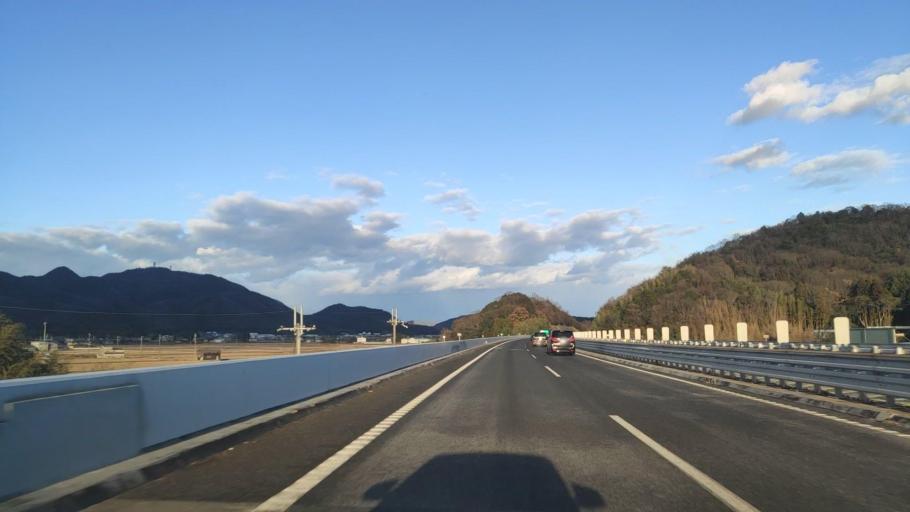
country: JP
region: Hyogo
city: Tatsunocho-tominaga
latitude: 34.8435
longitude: 134.5168
